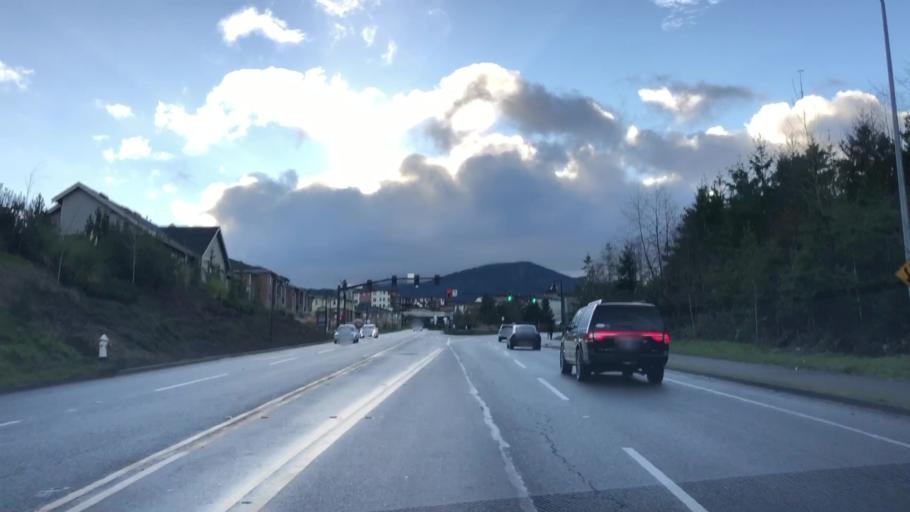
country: US
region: Washington
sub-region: King County
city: Issaquah
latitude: 47.5482
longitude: -122.0214
